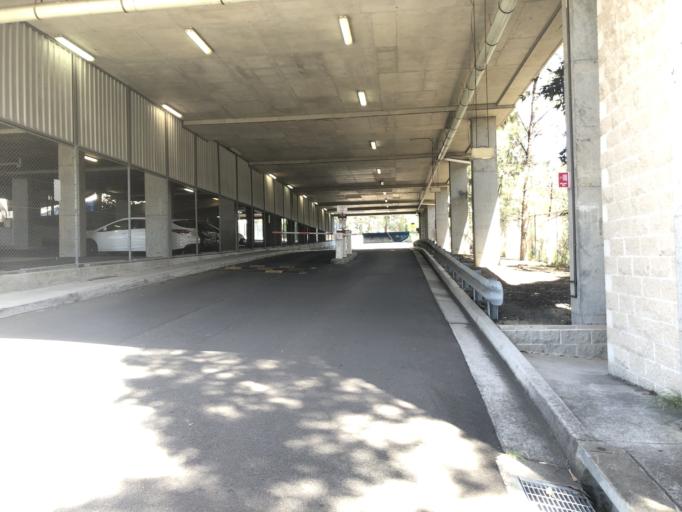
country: AU
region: New South Wales
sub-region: Willoughby
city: Artarmon
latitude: -33.8191
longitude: 151.1890
